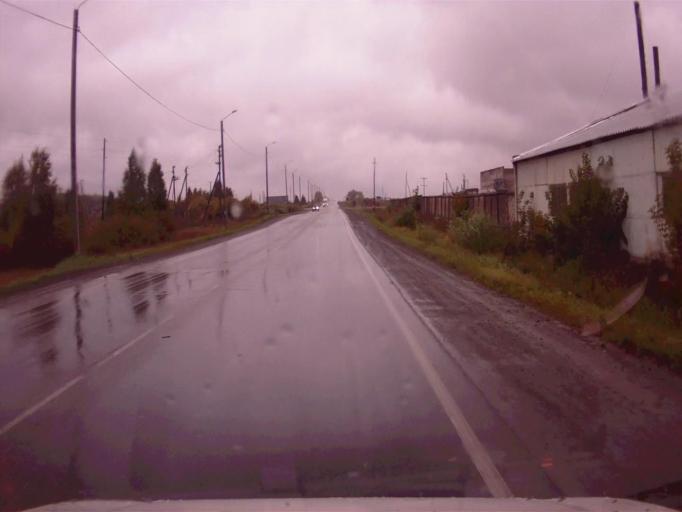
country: RU
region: Chelyabinsk
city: Argayash
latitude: 55.4773
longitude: 60.8637
